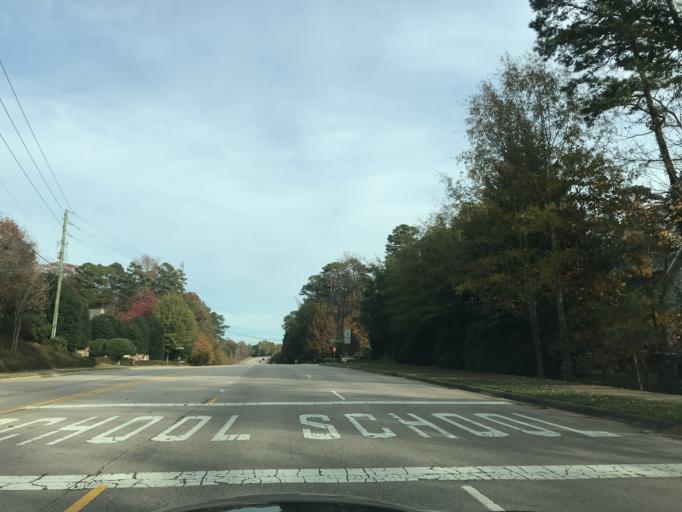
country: US
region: North Carolina
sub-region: Wake County
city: West Raleigh
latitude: 35.9021
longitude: -78.6681
